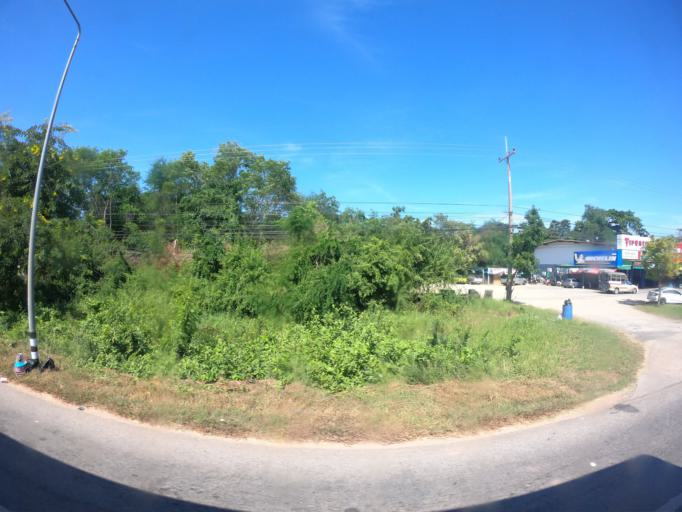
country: TH
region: Nakhon Ratchasima
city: Nakhon Ratchasima
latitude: 15.0426
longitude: 102.1498
